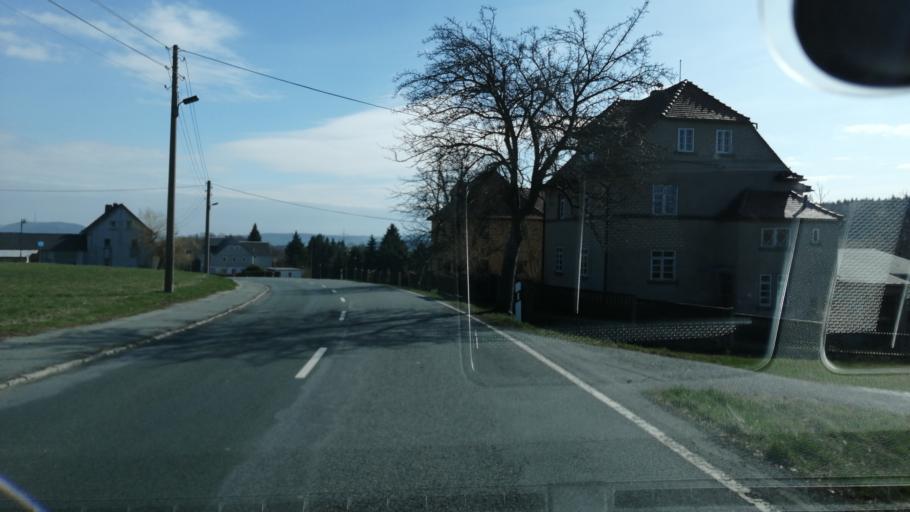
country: DE
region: Saxony
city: Schonbach
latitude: 51.0804
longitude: 14.5797
